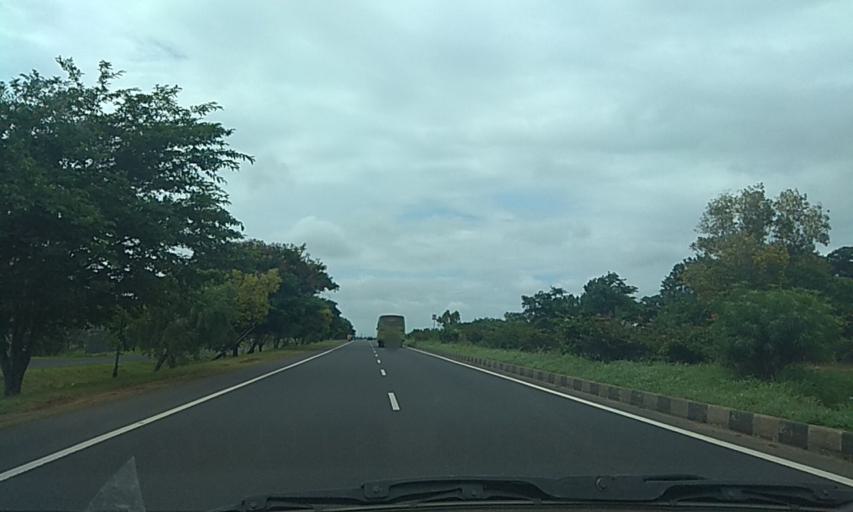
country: IN
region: Maharashtra
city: Nipani
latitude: 16.3735
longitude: 74.3977
